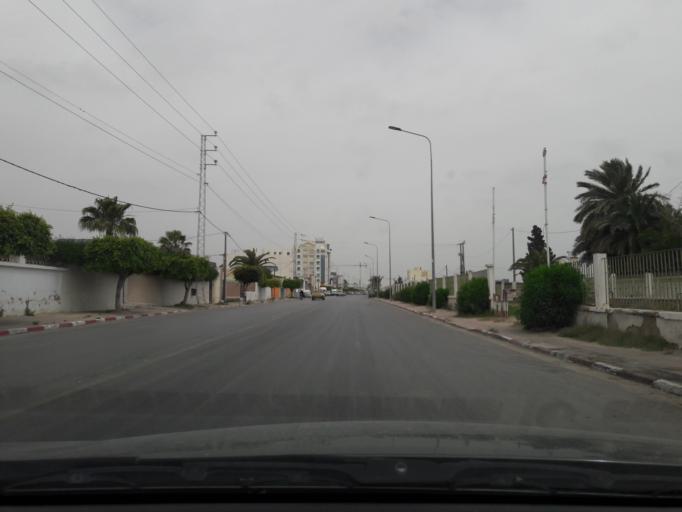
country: TN
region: Safaqis
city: Al Qarmadah
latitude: 34.7795
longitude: 10.7606
